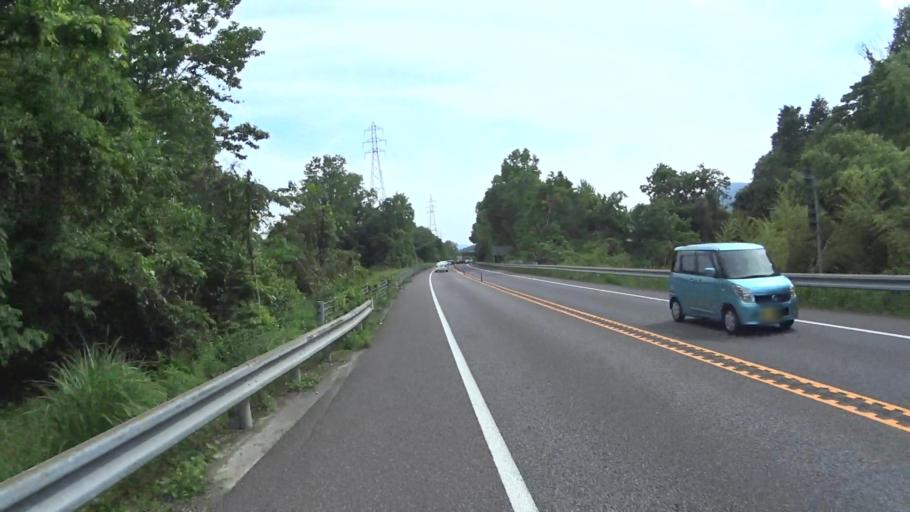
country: JP
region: Shiga Prefecture
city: Kitahama
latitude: 35.1146
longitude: 135.8981
